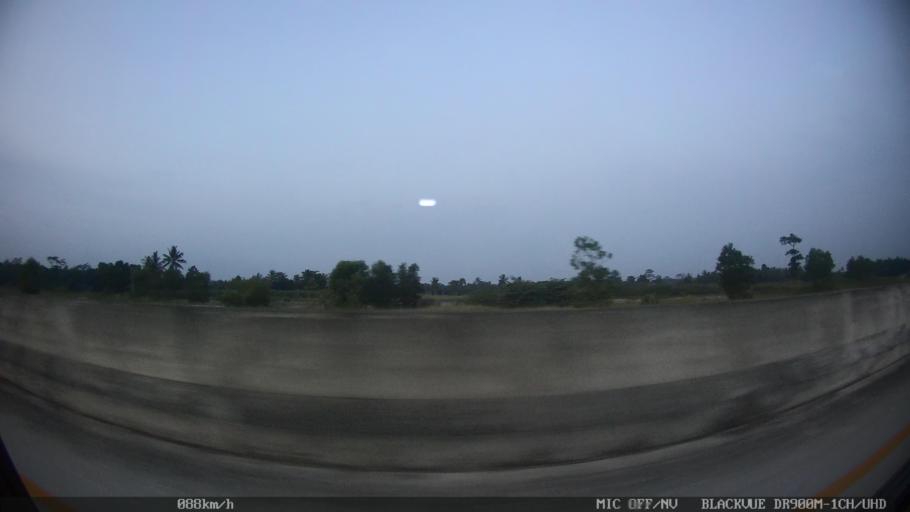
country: ID
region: Lampung
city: Sidorejo
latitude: -5.6423
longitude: 105.5738
